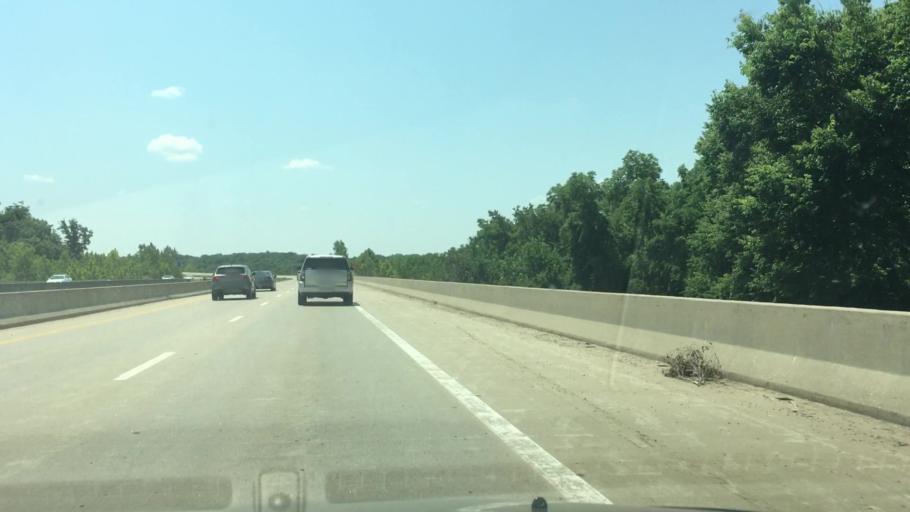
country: US
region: Missouri
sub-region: Jackson County
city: Grandview
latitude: 38.8686
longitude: -94.6015
